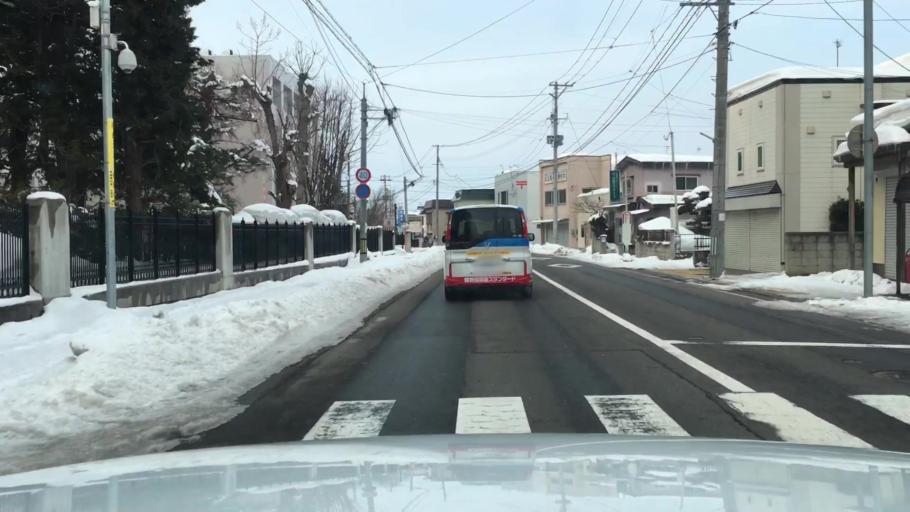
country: JP
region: Aomori
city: Hirosaki
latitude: 40.5871
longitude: 140.4747
